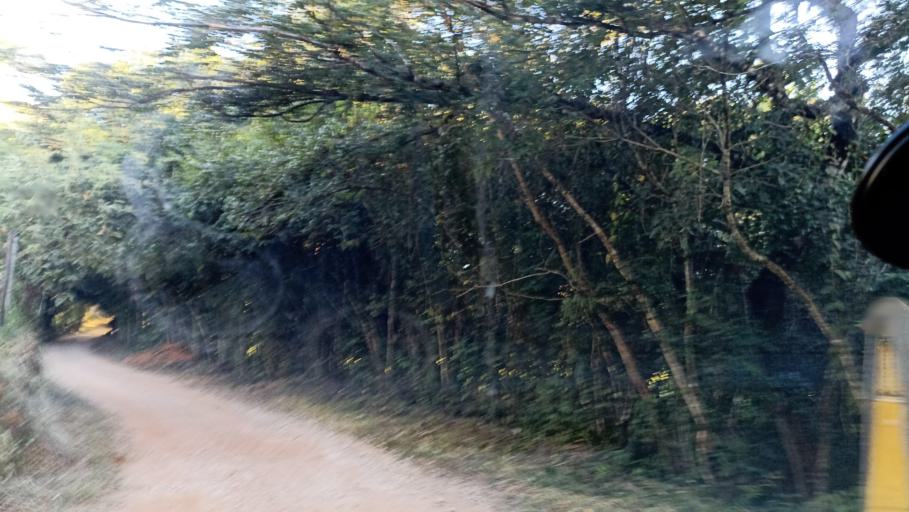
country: BR
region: Minas Gerais
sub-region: Sao Joao Del Rei
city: Sao Joao del Rei
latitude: -21.1804
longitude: -44.3550
